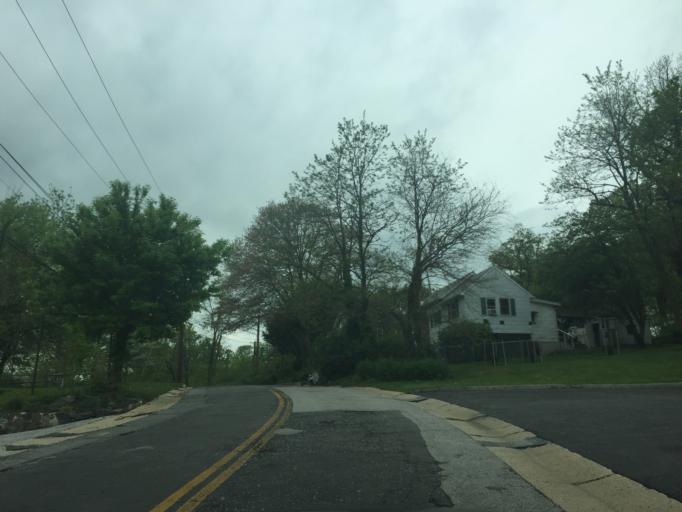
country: US
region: Maryland
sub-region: Baltimore County
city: Woodlawn
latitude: 39.3035
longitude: -76.7108
